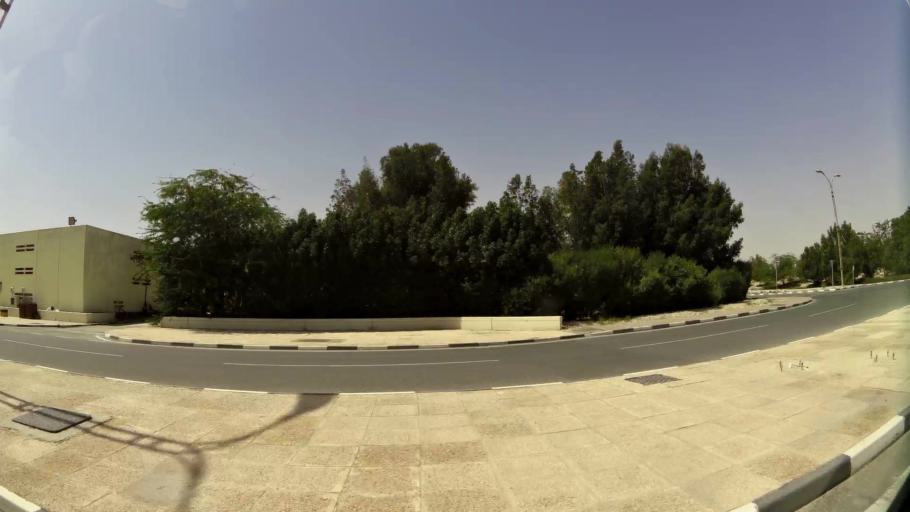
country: QA
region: Baladiyat ad Dawhah
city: Doha
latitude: 25.3690
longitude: 51.4942
